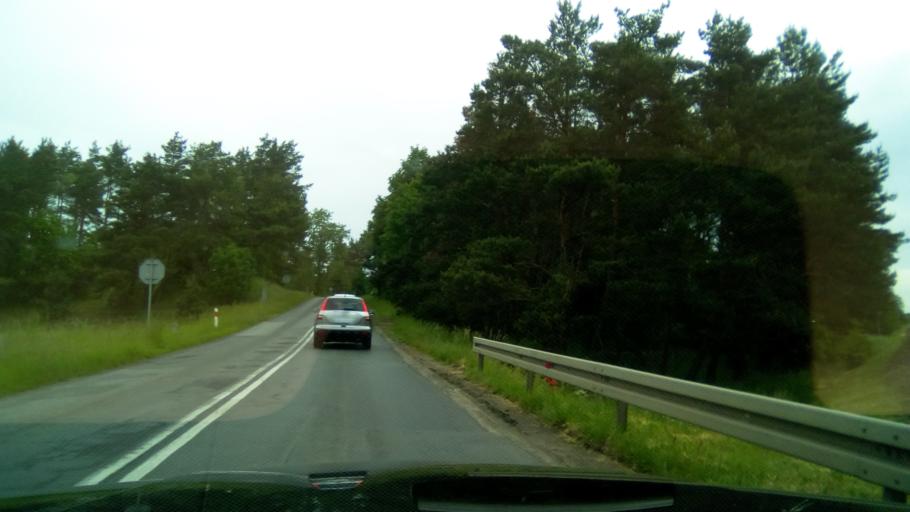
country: PL
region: Kujawsko-Pomorskie
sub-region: Powiat sepolenski
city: Wiecbork
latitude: 53.3689
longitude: 17.4971
